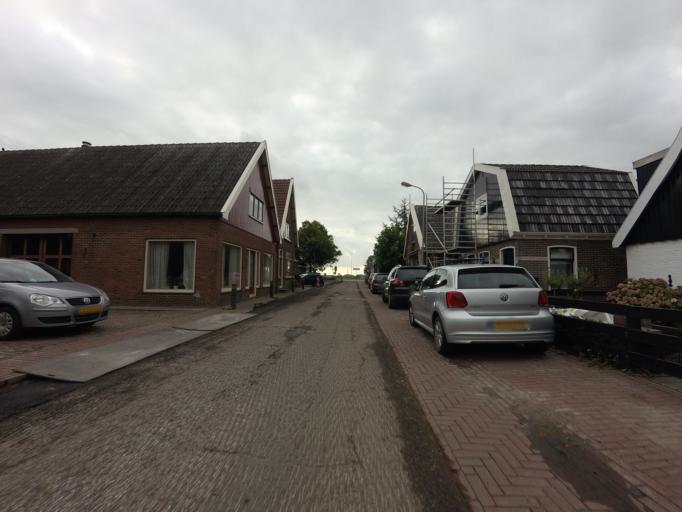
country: NL
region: North Holland
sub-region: Gemeente Medemblik
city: Opperdoes
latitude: 52.7248
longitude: 5.0765
